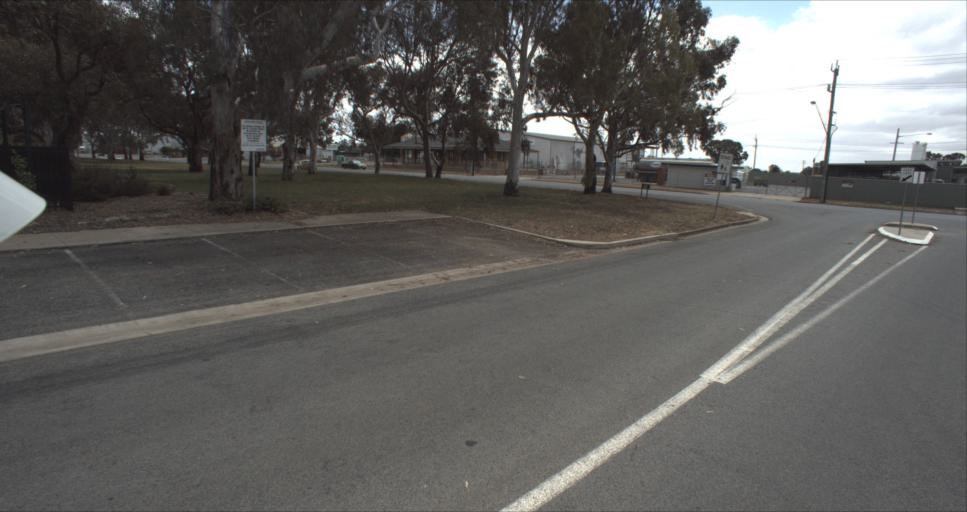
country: AU
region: New South Wales
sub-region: Leeton
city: Leeton
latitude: -34.5542
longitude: 146.3929
